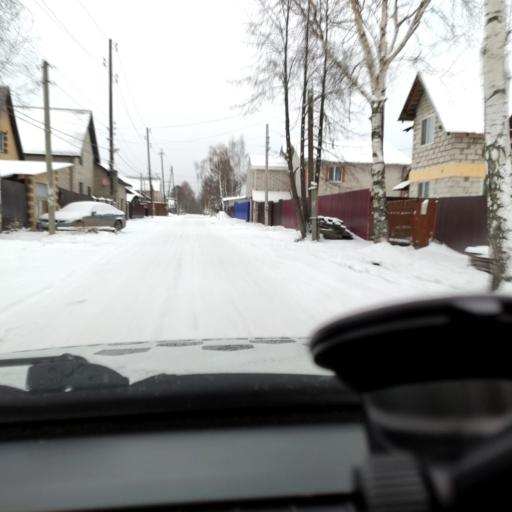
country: RU
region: Perm
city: Perm
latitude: 58.0601
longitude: 56.3646
